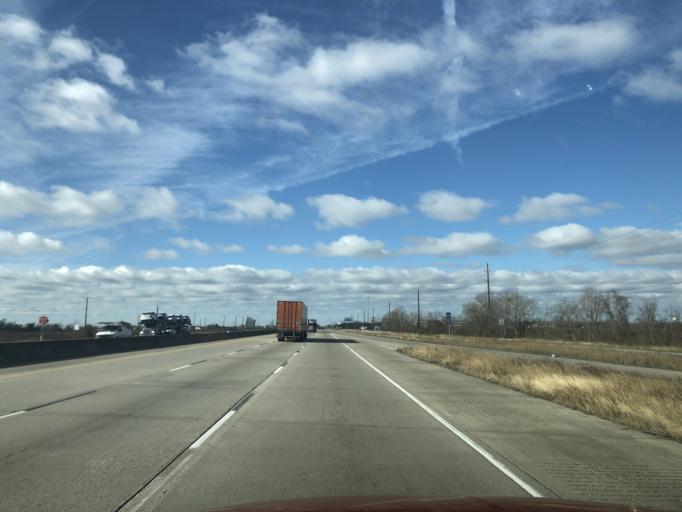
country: US
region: Texas
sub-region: Chambers County
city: Old River-Winfree
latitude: 29.8297
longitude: -94.8076
